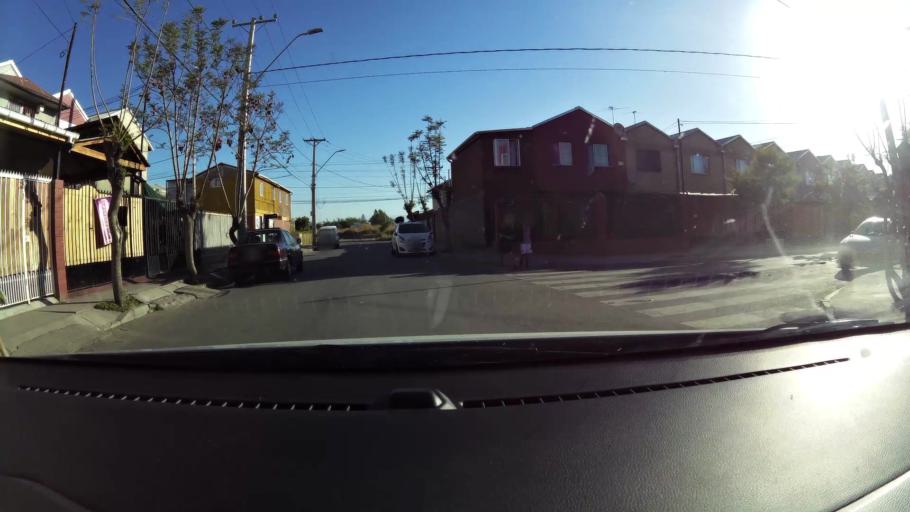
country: CL
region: Santiago Metropolitan
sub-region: Provincia de Maipo
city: San Bernardo
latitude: -33.6041
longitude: -70.6755
